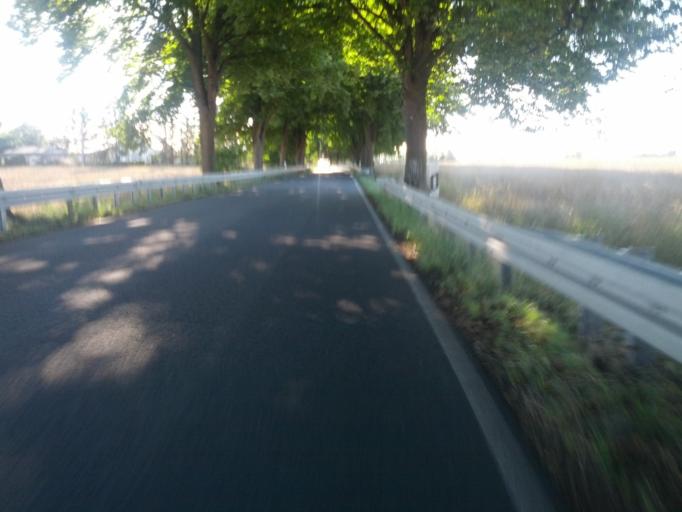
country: DE
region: Mecklenburg-Vorpommern
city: Bastorf
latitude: 54.1078
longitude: 11.6487
